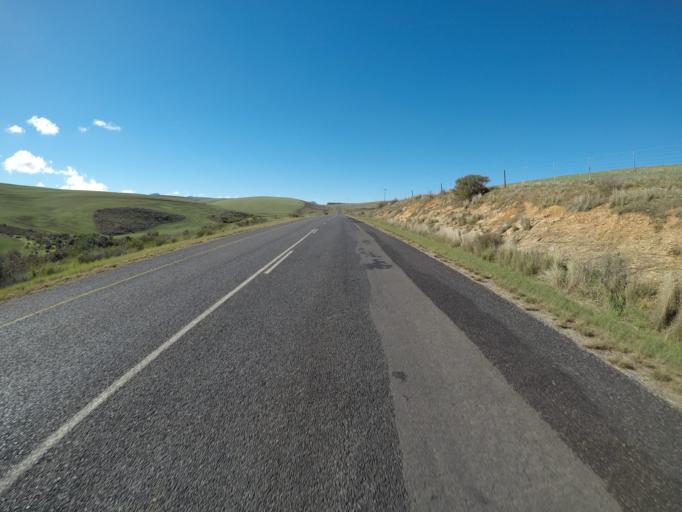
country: ZA
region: Western Cape
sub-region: Overberg District Municipality
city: Caledon
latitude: -34.1504
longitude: 19.4797
